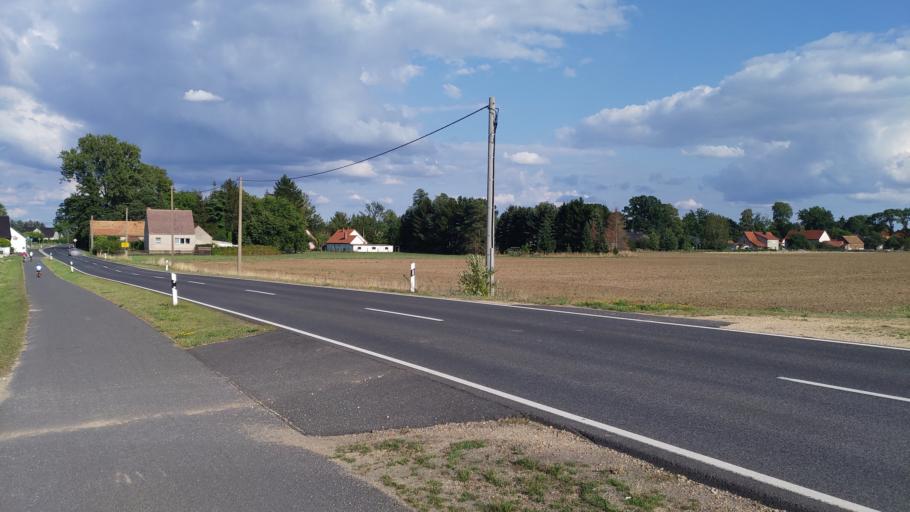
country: DE
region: Saxony
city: Horka
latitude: 51.2924
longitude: 14.8863
